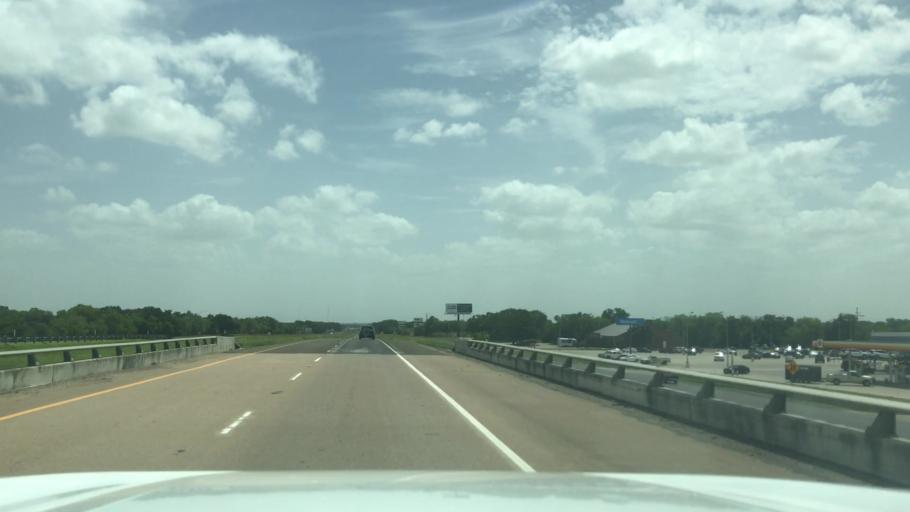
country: US
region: Texas
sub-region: Falls County
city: Marlin
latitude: 31.3064
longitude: -96.8748
